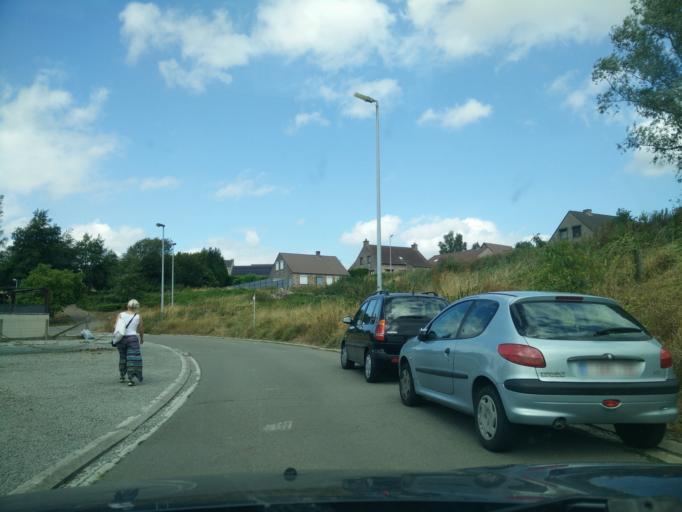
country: BE
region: Flanders
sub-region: Provincie Vlaams-Brabant
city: Halle
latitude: 50.7173
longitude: 4.2145
